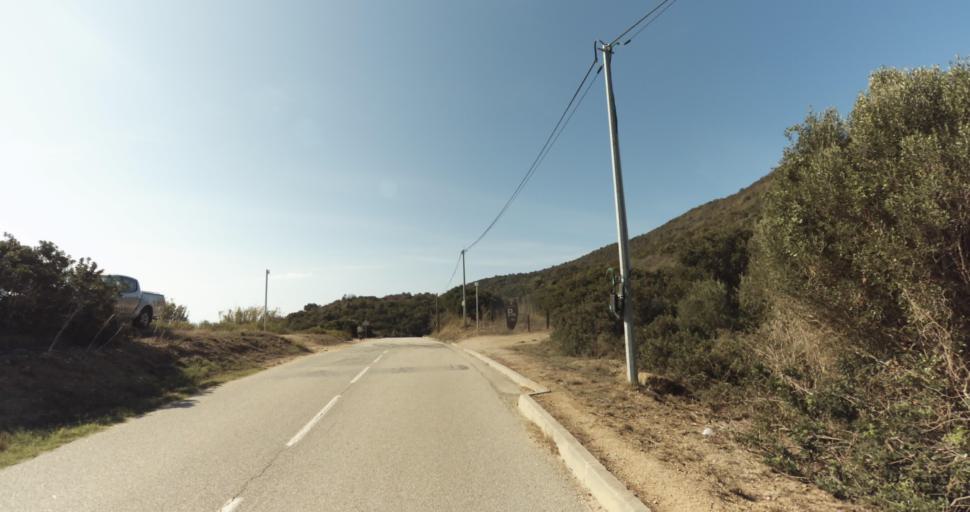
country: FR
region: Corsica
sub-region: Departement de la Corse-du-Sud
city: Ajaccio
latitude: 41.9220
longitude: 8.6426
